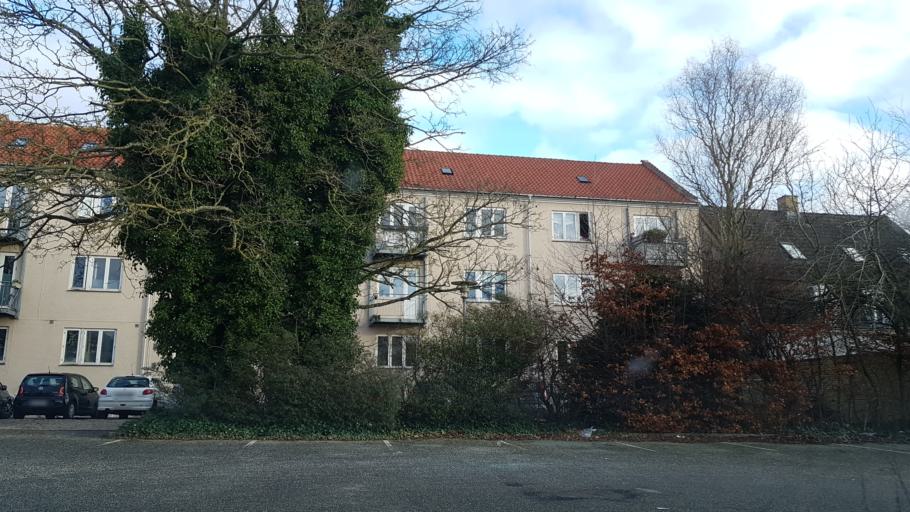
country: DK
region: Zealand
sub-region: Slagelse Kommune
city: Slagelse
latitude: 55.4022
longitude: 11.3563
